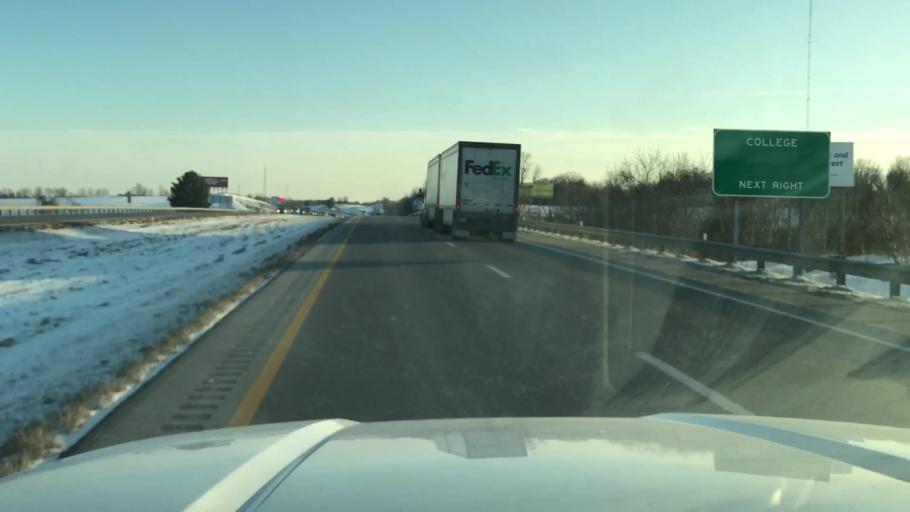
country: US
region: Missouri
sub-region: Andrew County
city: Country Club Village
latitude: 39.8295
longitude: -94.8053
